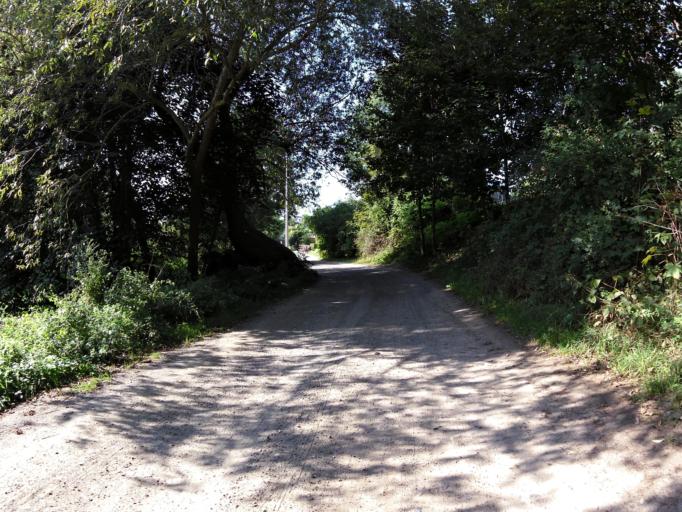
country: DE
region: Mecklenburg-Vorpommern
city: Seebad Bansin
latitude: 53.9589
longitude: 14.1408
